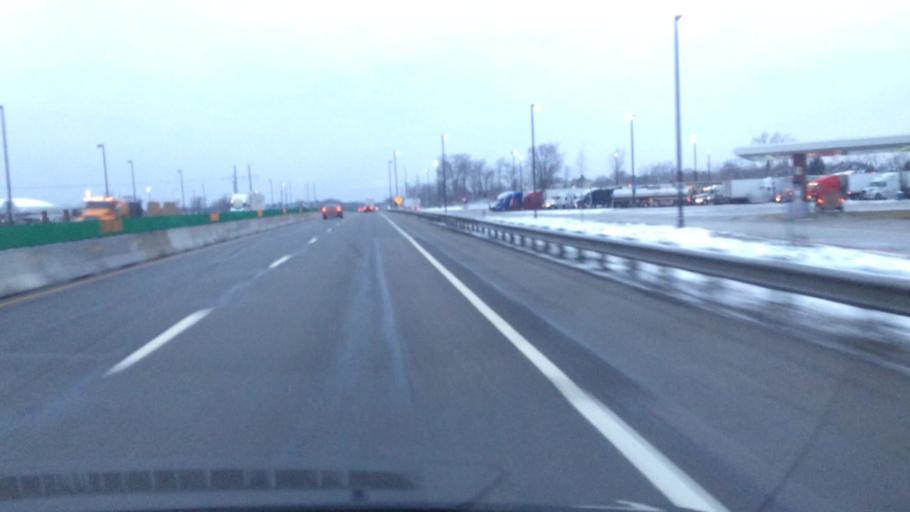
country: US
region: Ohio
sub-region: Cuyahoga County
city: Broadview Heights
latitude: 41.2917
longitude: -81.6719
